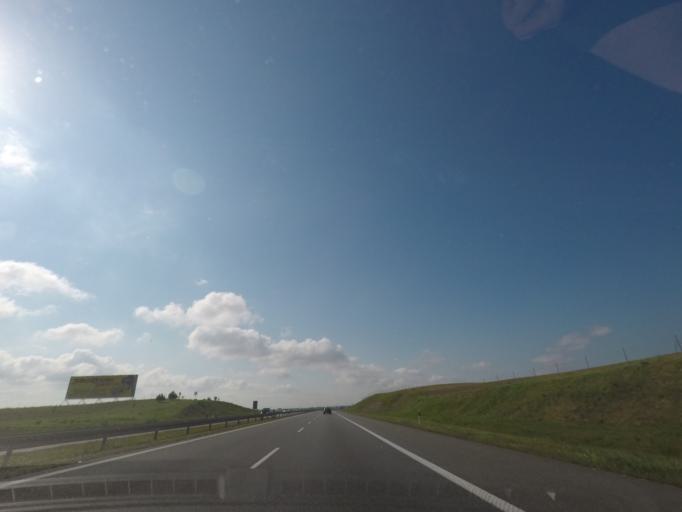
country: PL
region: Pomeranian Voivodeship
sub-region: Powiat gdanski
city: Pszczolki
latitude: 54.1689
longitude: 18.6538
